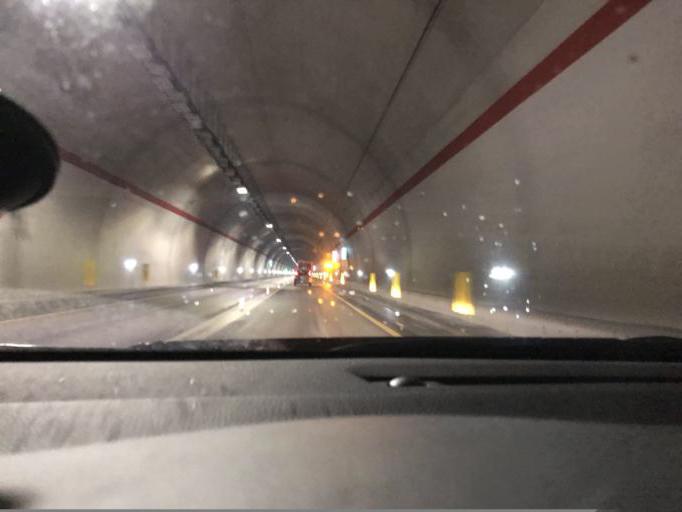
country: IT
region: The Marches
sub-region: Provincia di Ancona
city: Cerreto d'Esi
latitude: 43.3503
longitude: 12.9946
